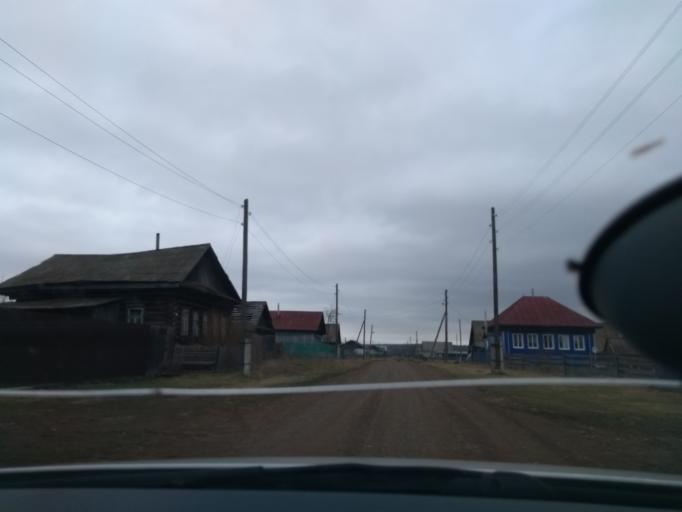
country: RU
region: Perm
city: Orda
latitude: 57.2207
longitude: 56.5939
